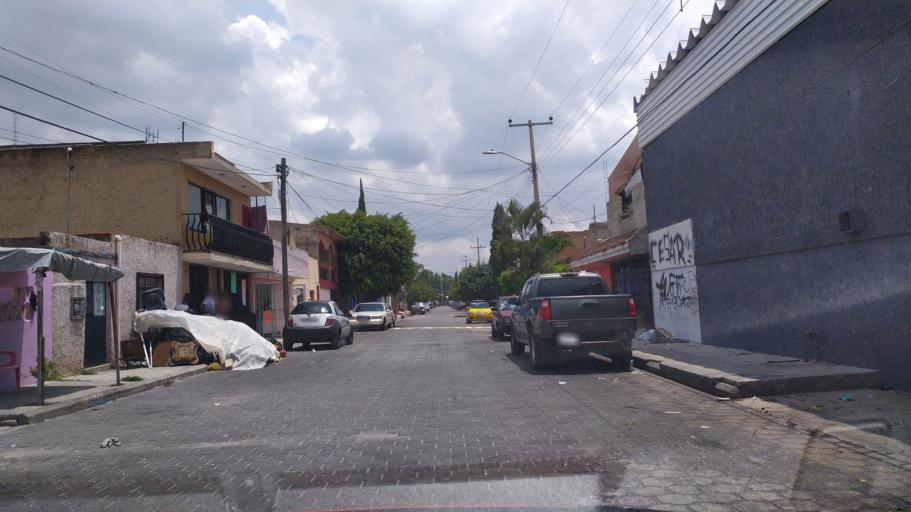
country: MX
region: Jalisco
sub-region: Tlajomulco de Zuniga
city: Palomar
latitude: 20.6379
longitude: -103.4515
